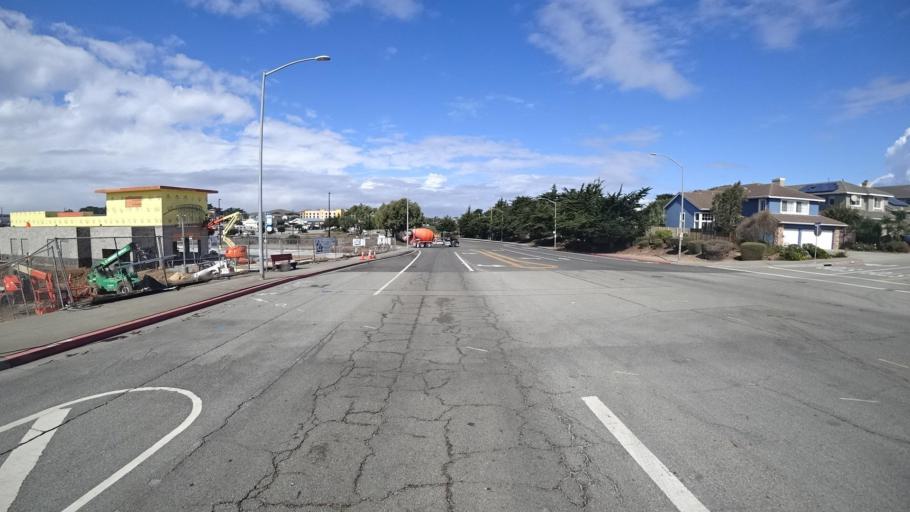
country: US
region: California
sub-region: Monterey County
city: Marina
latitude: 36.6942
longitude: -121.7989
